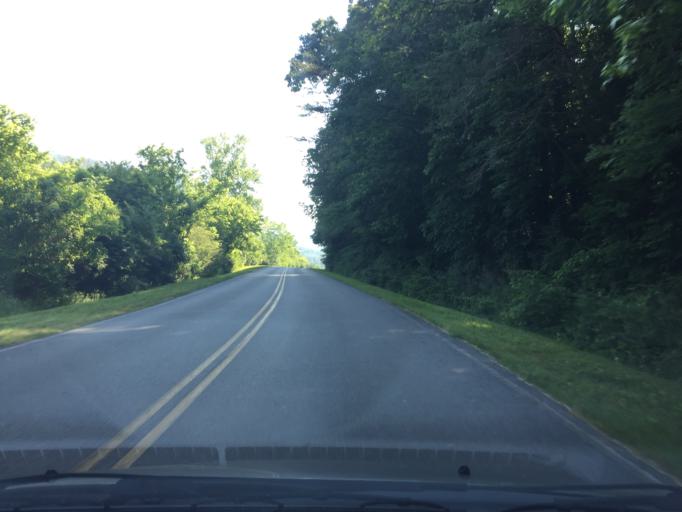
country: US
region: Tennessee
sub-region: Hamilton County
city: Lookout Mountain
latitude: 35.0585
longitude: -85.4179
